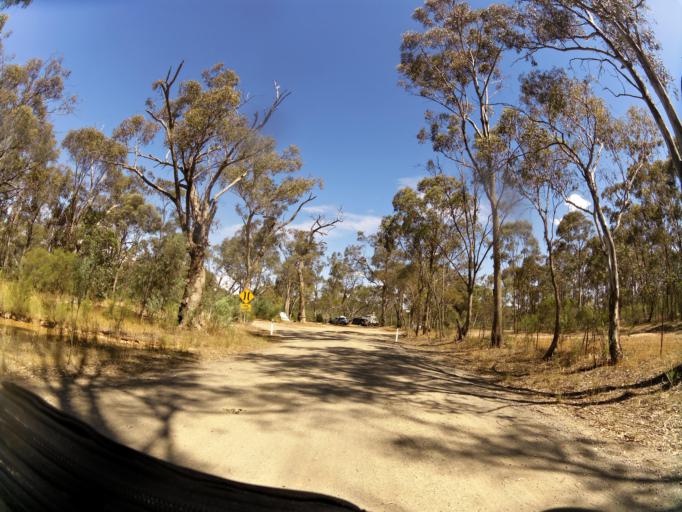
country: AU
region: Victoria
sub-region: Campaspe
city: Kyabram
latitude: -36.8549
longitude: 145.0669
